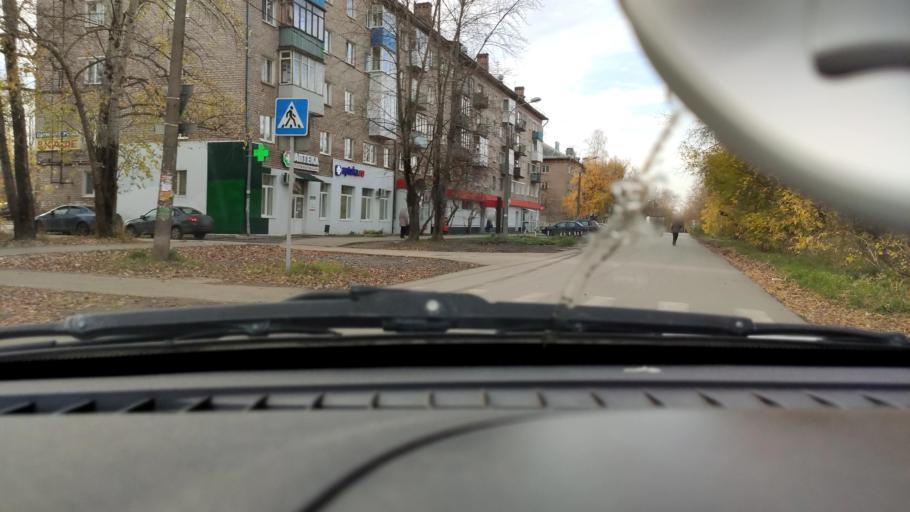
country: RU
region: Perm
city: Perm
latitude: 58.0885
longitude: 56.3922
